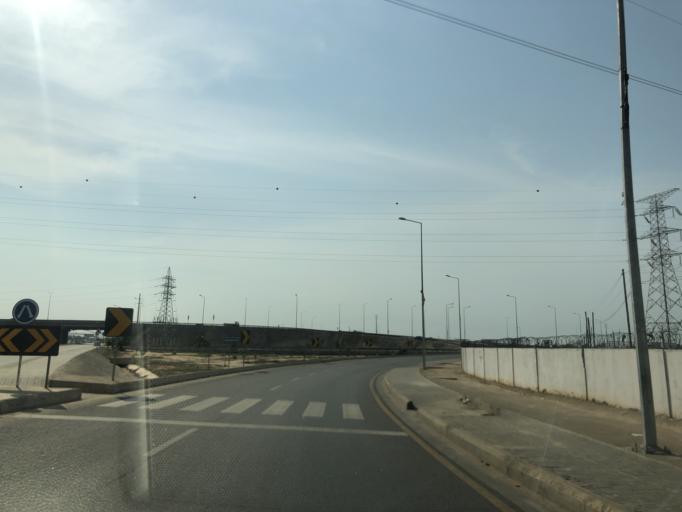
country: AO
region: Luanda
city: Luanda
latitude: -8.9729
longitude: 13.2565
